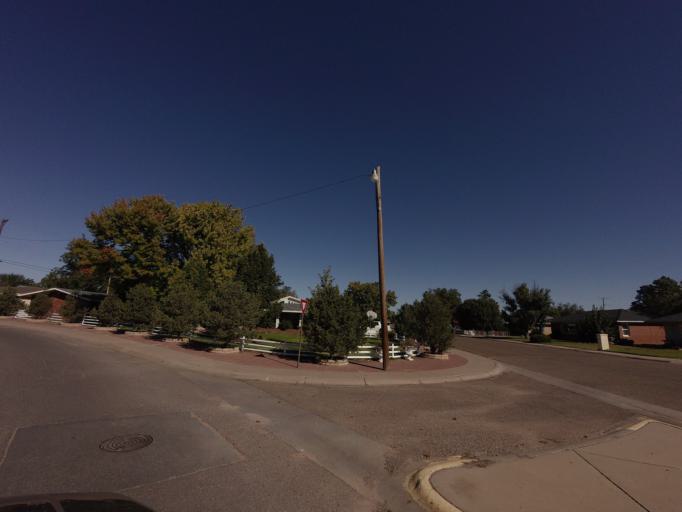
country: US
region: New Mexico
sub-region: Curry County
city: Clovis
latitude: 34.4277
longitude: -103.2017
